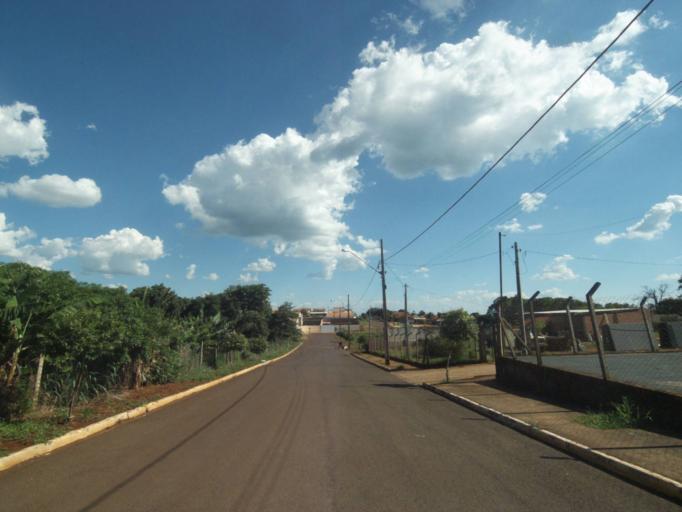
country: BR
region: Parana
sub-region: Sertanopolis
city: Sertanopolis
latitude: -23.0431
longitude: -50.8184
